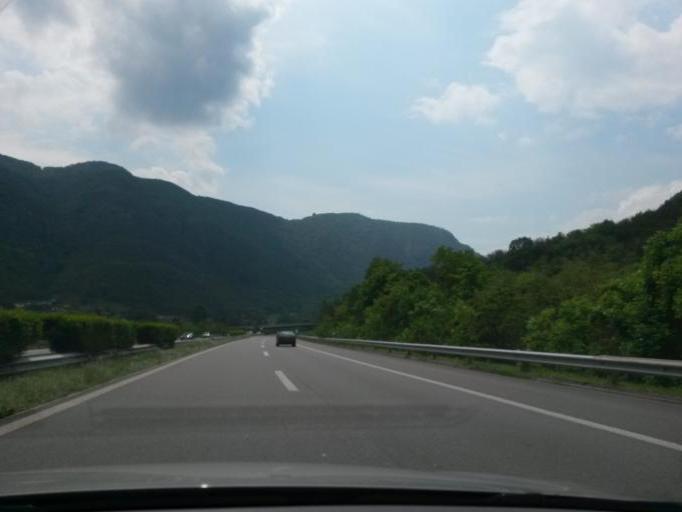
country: CH
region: Ticino
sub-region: Bellinzona District
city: Cadenazzo
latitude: 46.1126
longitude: 8.9291
